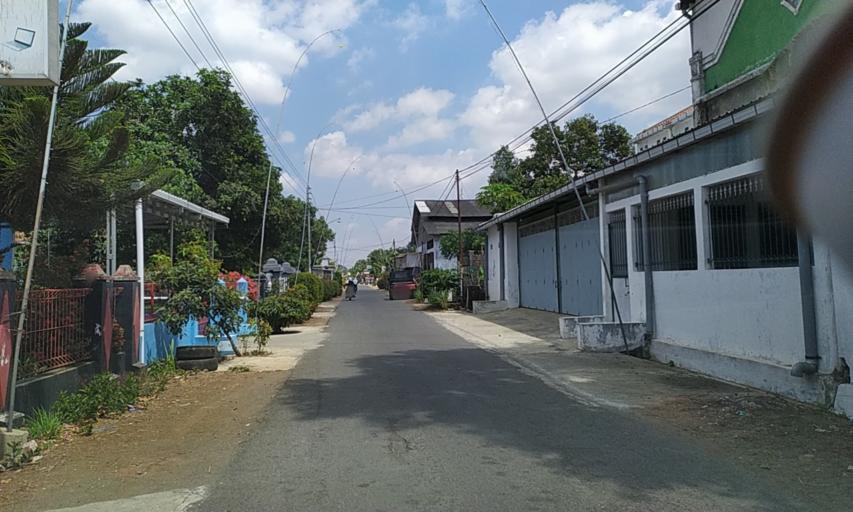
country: ID
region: Central Java
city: Kroya
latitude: -7.6333
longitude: 109.2477
